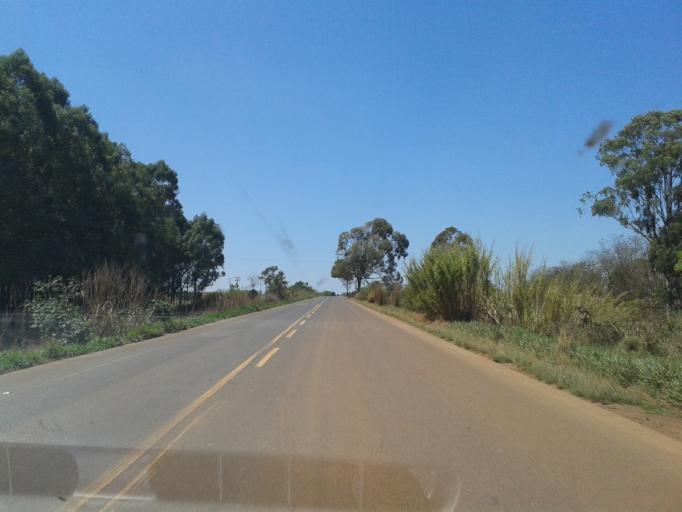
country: BR
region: Minas Gerais
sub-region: Araxa
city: Araxa
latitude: -19.4117
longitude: -47.3049
